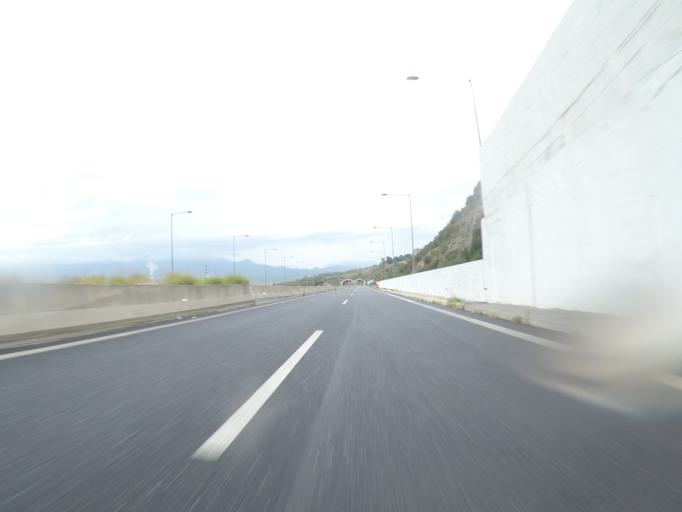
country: GR
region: Peloponnese
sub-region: Nomos Arkadias
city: Megalopoli
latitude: 37.3891
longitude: 22.1902
